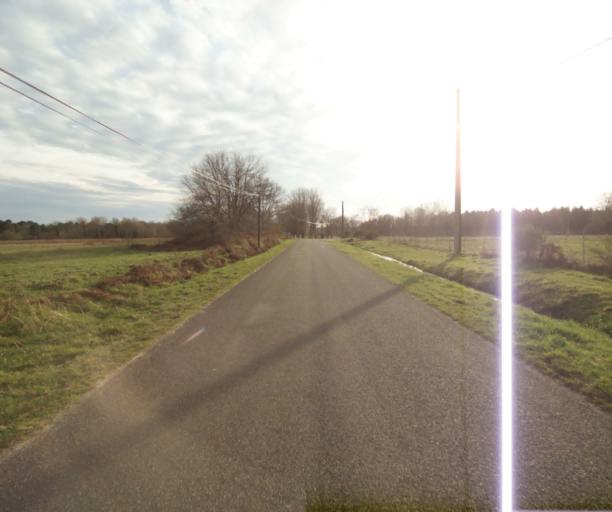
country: FR
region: Aquitaine
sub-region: Departement des Landes
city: Gabarret
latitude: 44.0328
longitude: 0.0604
